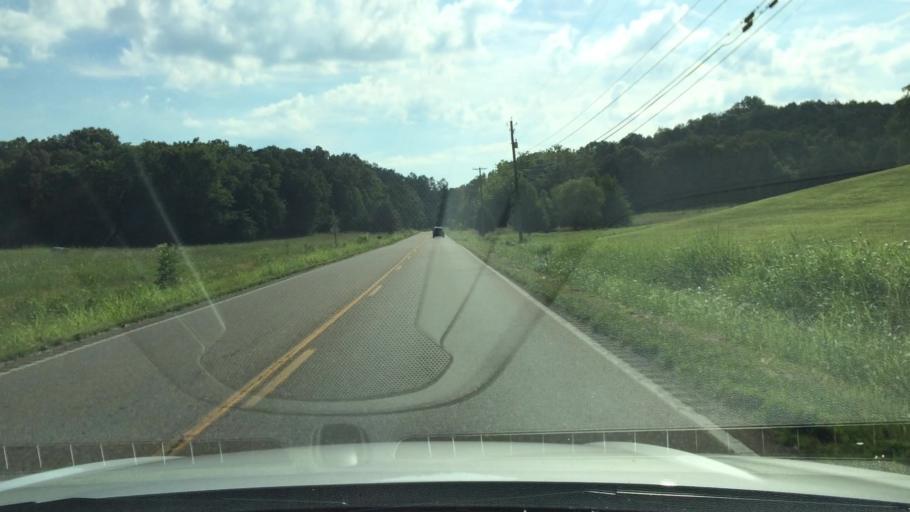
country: US
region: Tennessee
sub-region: Sevier County
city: Sevierville
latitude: 35.9206
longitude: -83.6176
